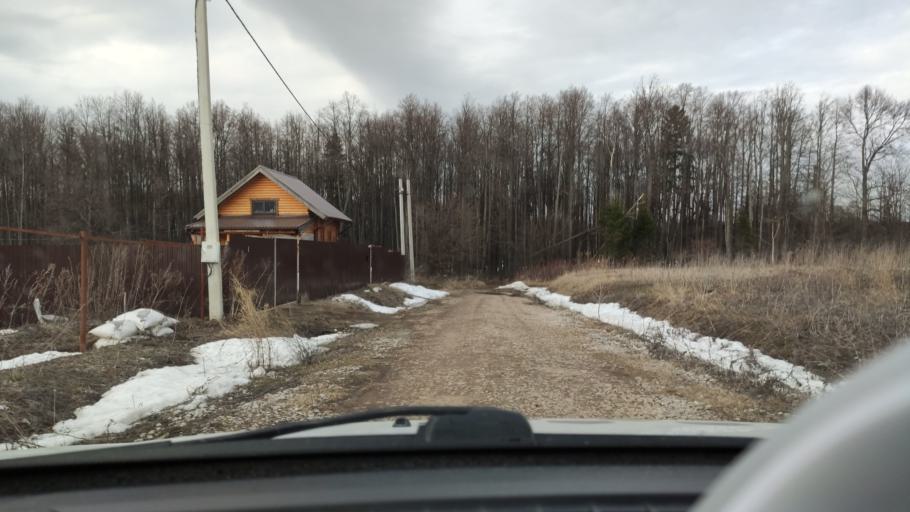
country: RU
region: Perm
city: Ferma
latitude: 57.8837
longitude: 56.3386
